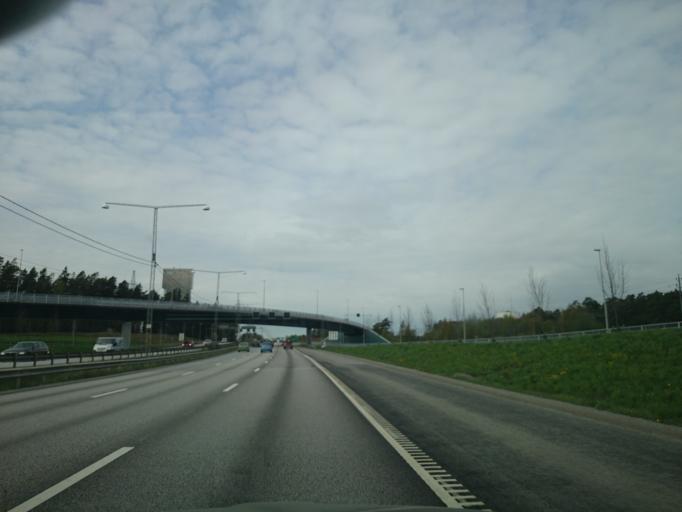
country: SE
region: Stockholm
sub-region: Stockholms Kommun
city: Kista
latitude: 59.4033
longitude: 17.9708
